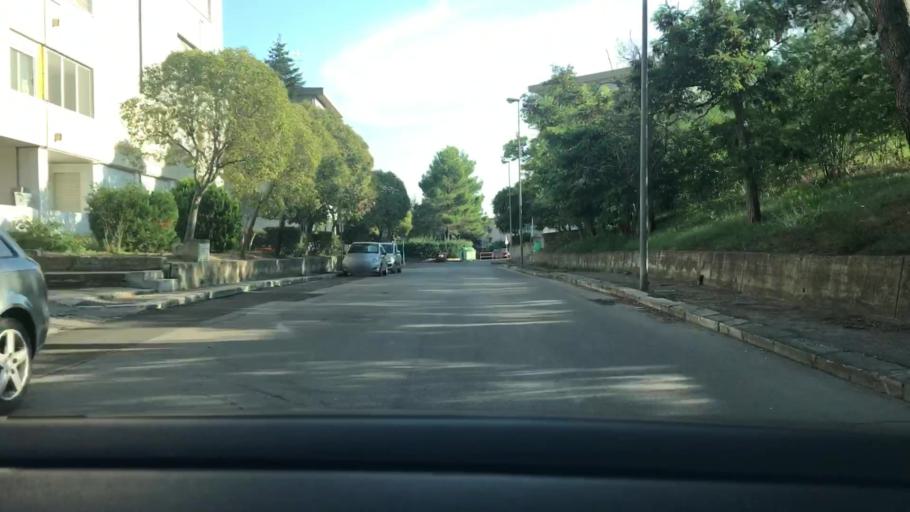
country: IT
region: Basilicate
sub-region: Provincia di Matera
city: Matera
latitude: 40.6870
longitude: 16.5856
